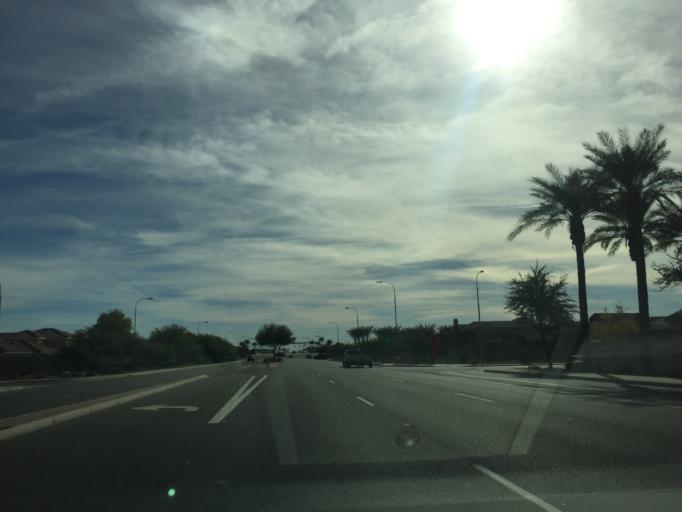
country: US
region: Arizona
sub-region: Maricopa County
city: Chandler
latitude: 33.2871
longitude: -111.8070
